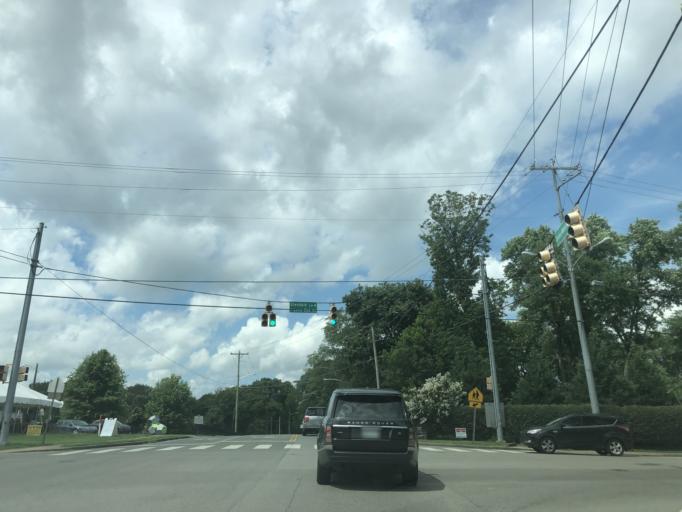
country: US
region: Tennessee
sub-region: Davidson County
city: Oak Hill
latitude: 36.0945
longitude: -86.8013
